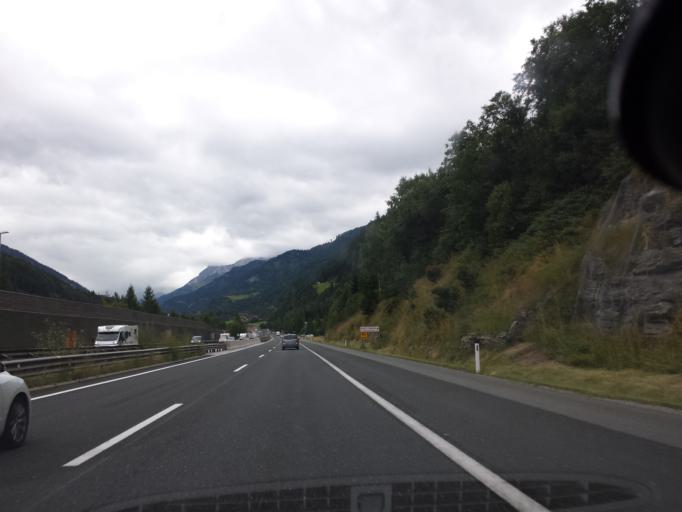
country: AT
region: Salzburg
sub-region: Politischer Bezirk Tamsweg
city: Sankt Michael im Lungau
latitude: 47.1075
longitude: 13.5941
